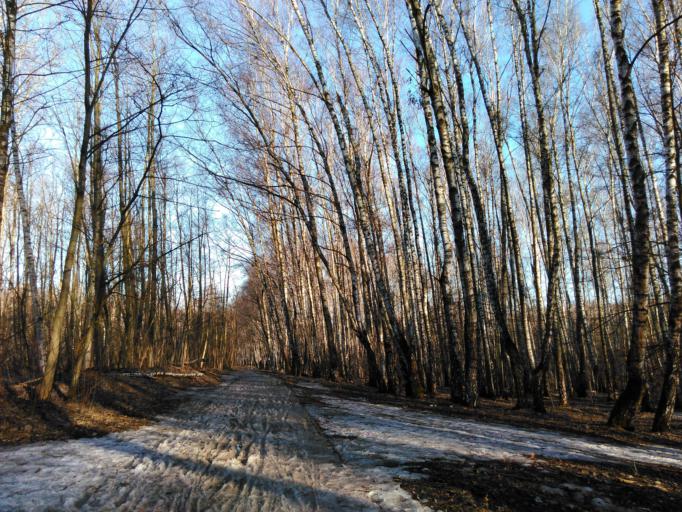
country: RU
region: Moscow
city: Zyuzino
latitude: 55.6319
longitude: 37.5813
